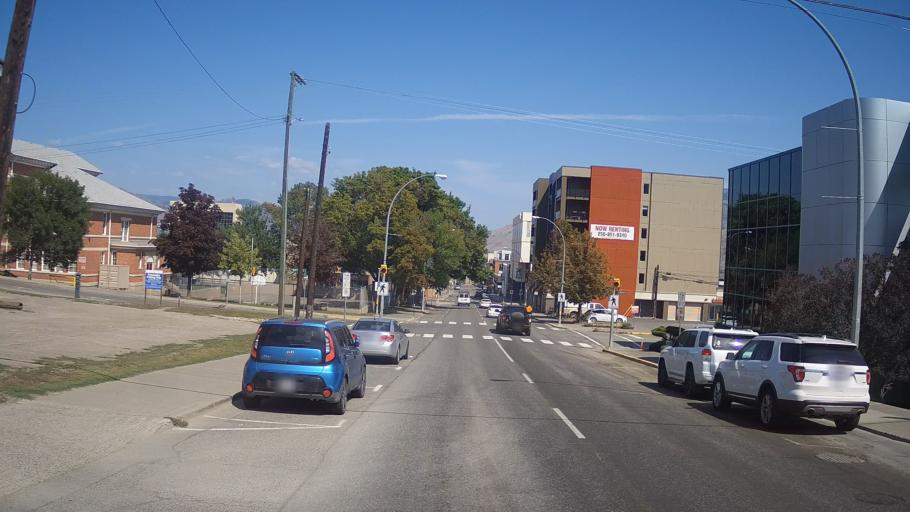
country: CA
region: British Columbia
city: Kamloops
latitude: 50.6727
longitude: -120.3345
